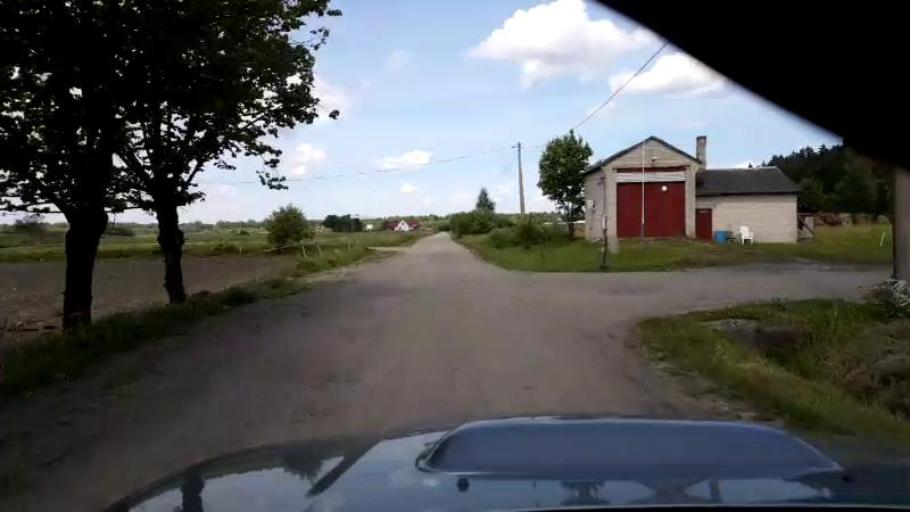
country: EE
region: Paernumaa
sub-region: Halinga vald
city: Parnu-Jaagupi
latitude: 58.5155
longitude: 24.5631
